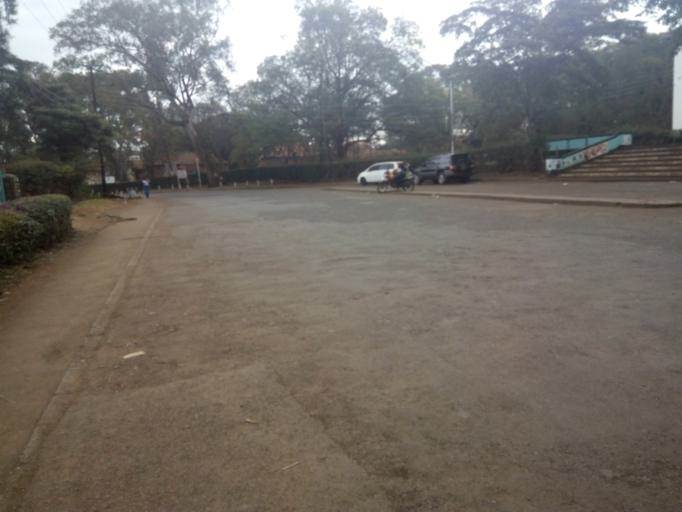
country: KE
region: Nairobi Area
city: Nairobi
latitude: -1.2836
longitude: 36.8118
